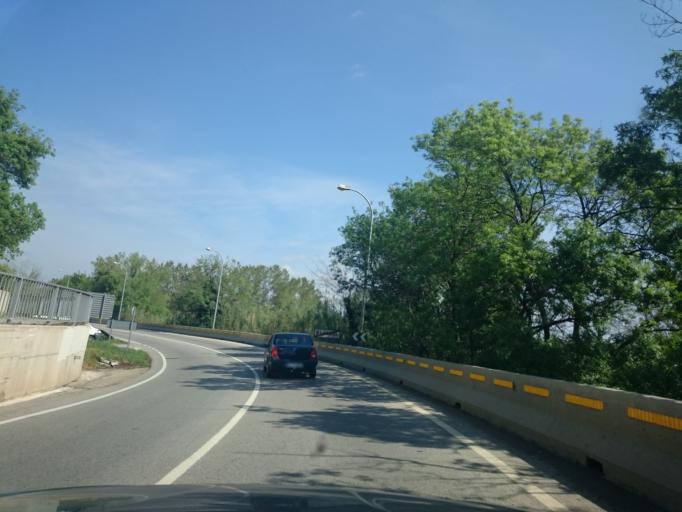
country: ES
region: Catalonia
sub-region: Provincia de Girona
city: Bascara
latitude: 42.1604
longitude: 2.9114
